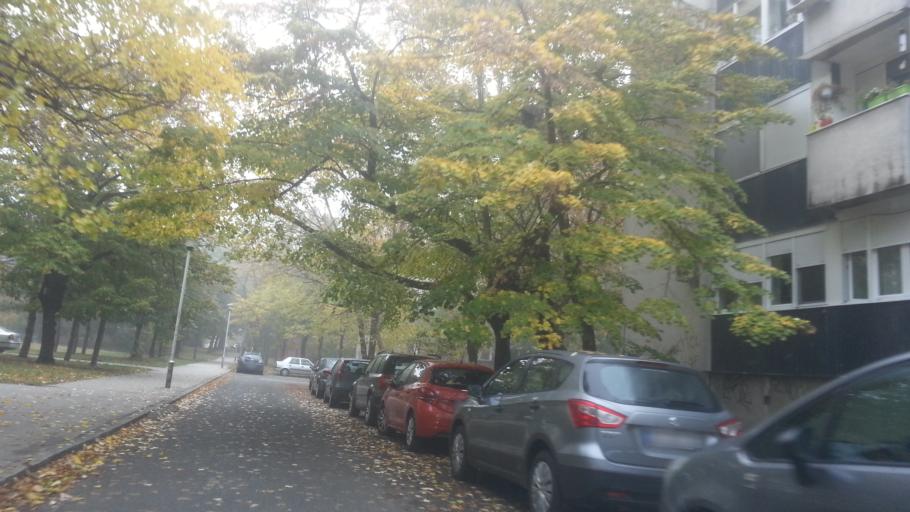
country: RS
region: Central Serbia
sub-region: Belgrade
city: Zemun
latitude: 44.8270
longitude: 20.4140
